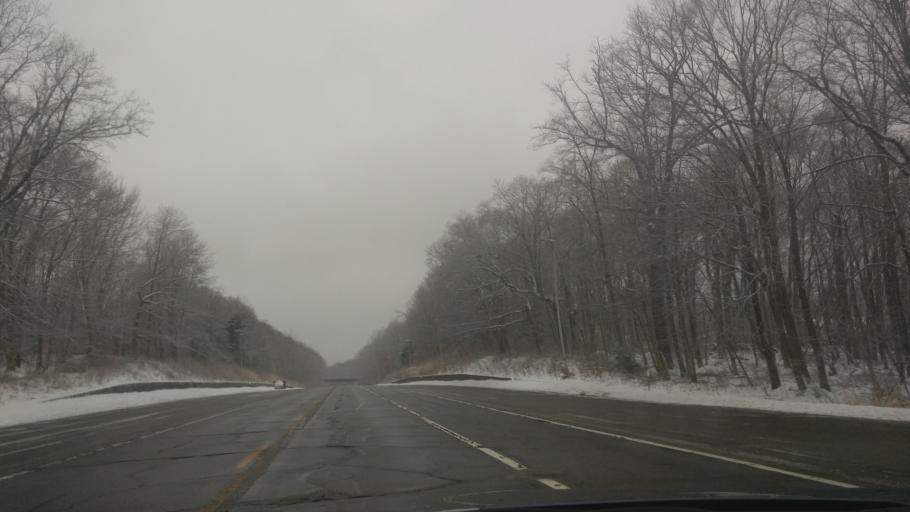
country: US
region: Rhode Island
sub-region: Providence County
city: North Scituate
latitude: 41.8376
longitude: -71.6318
